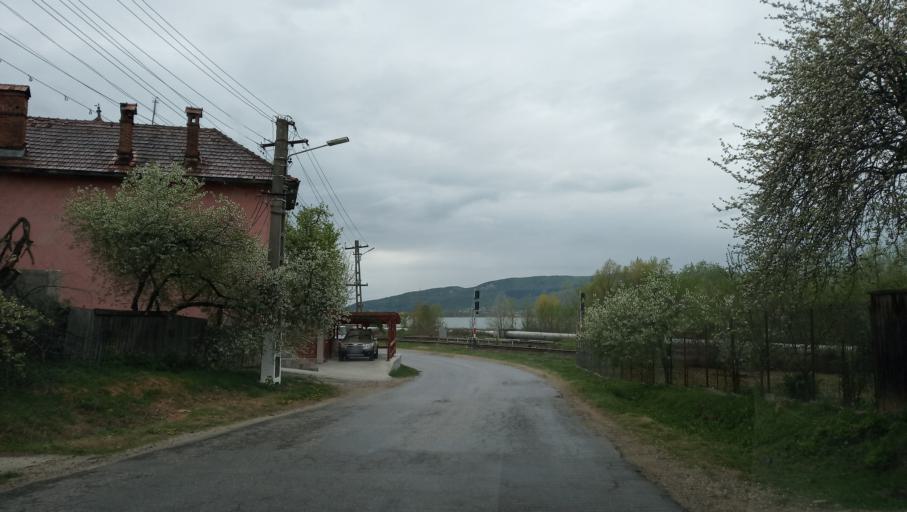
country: RO
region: Valcea
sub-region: Comuna Daesti
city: Daesti
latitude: 45.1965
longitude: 24.3840
